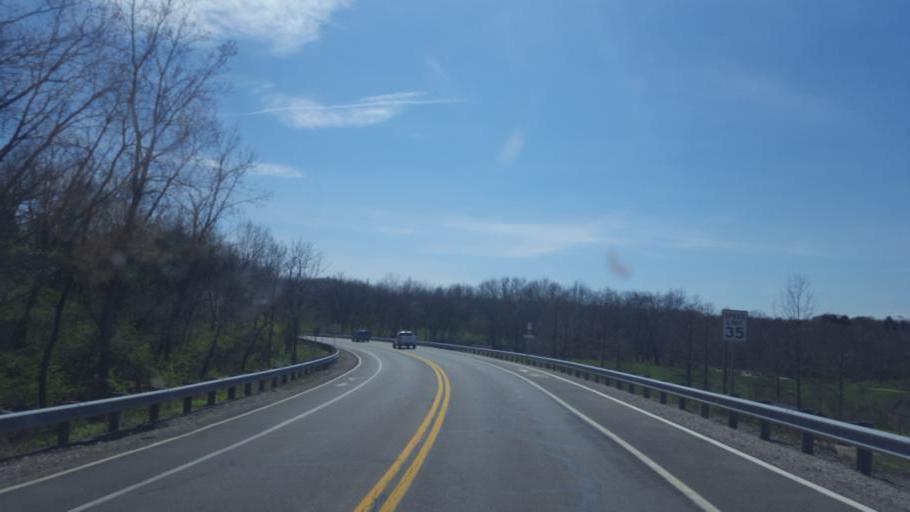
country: US
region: Ohio
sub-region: Franklin County
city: Worthington
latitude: 40.1099
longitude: -83.0306
